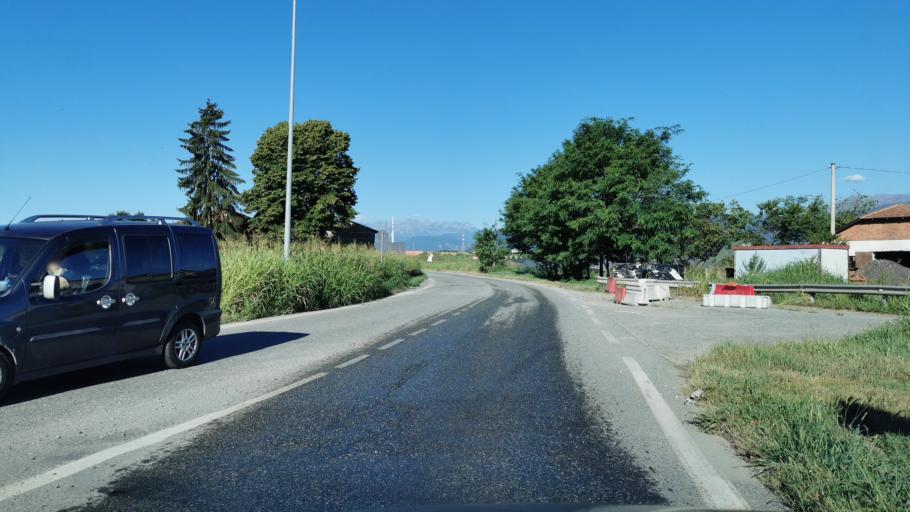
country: IT
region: Piedmont
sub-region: Provincia di Torino
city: Druento
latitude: 45.1171
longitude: 7.5896
